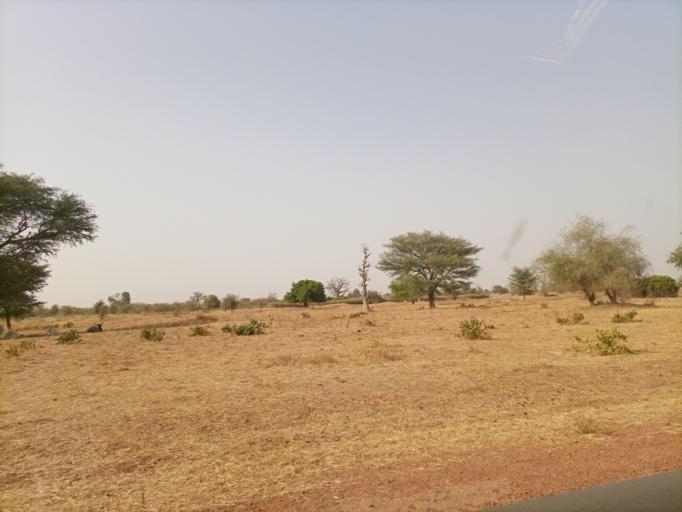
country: SN
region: Fatick
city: Foundiougne
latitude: 14.1284
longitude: -16.4102
